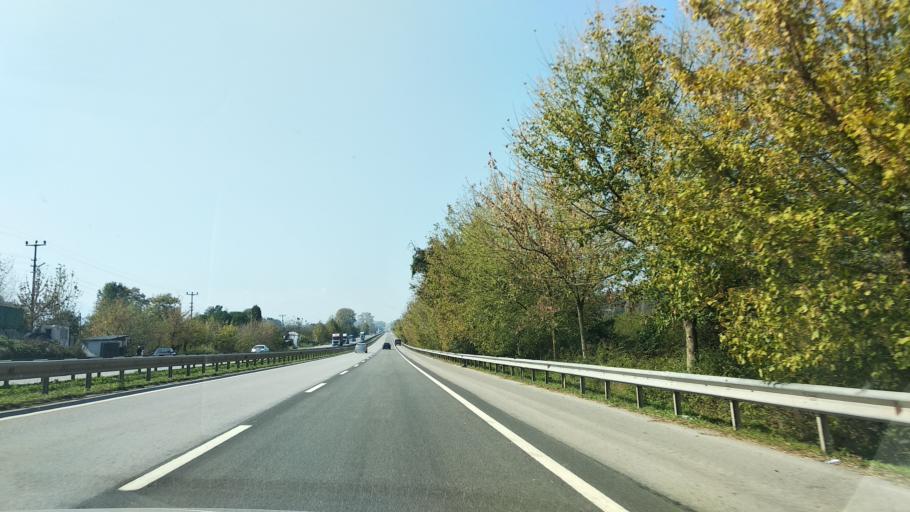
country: TR
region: Sakarya
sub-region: Merkez
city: Sapanca
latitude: 40.7330
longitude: 30.2110
